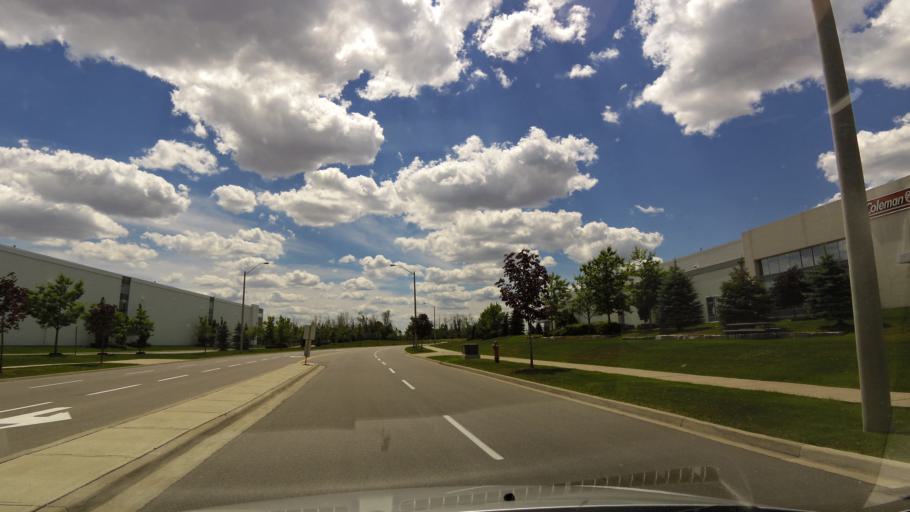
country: CA
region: Ontario
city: Brampton
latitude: 43.6185
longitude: -79.7761
